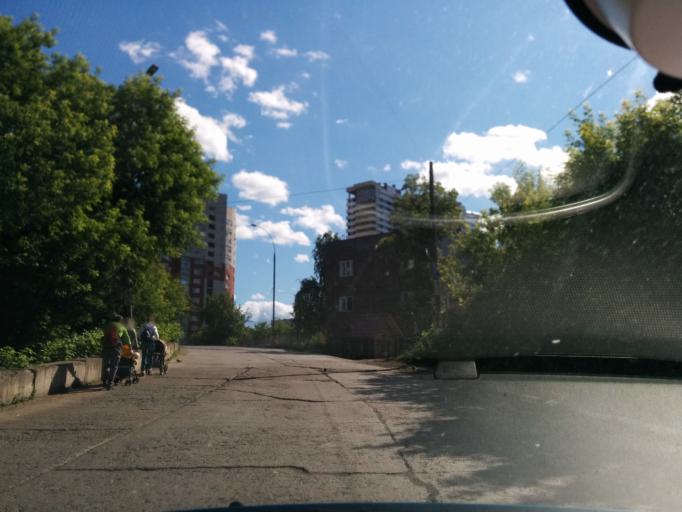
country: RU
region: Perm
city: Perm
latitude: 58.0129
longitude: 56.2044
